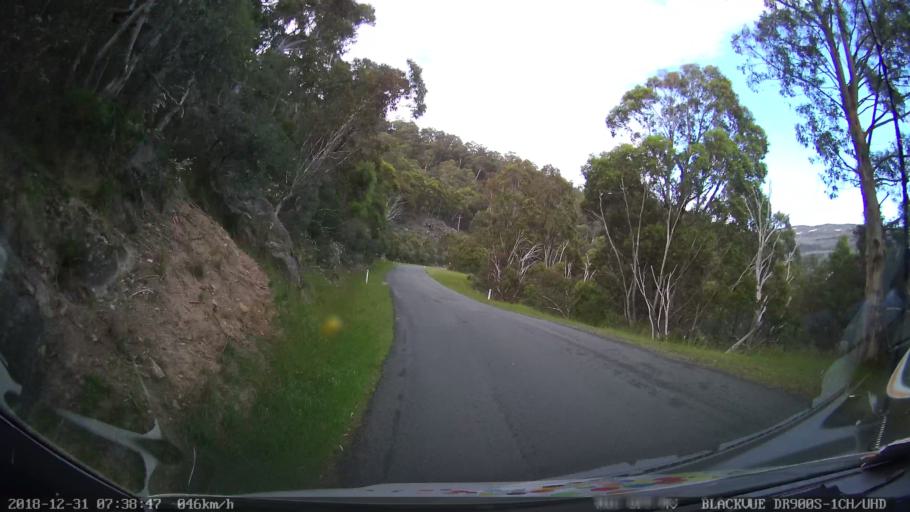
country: AU
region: New South Wales
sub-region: Snowy River
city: Jindabyne
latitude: -36.3488
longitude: 148.4260
